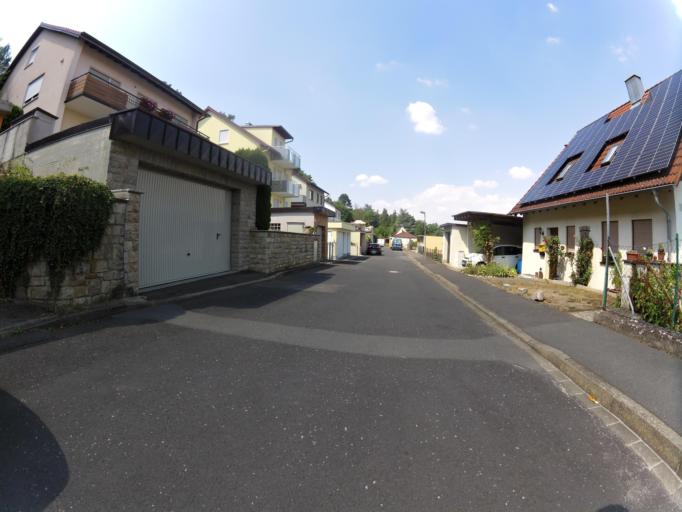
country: DE
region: Bavaria
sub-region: Regierungsbezirk Unterfranken
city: Ochsenfurt
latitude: 49.6599
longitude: 10.0580
